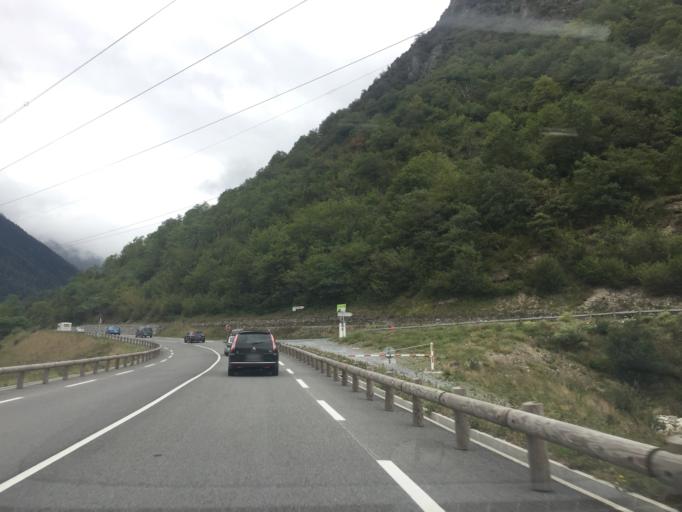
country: FR
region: Midi-Pyrenees
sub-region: Departement des Hautes-Pyrenees
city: Saint-Lary-Soulan
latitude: 42.8796
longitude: 0.3472
